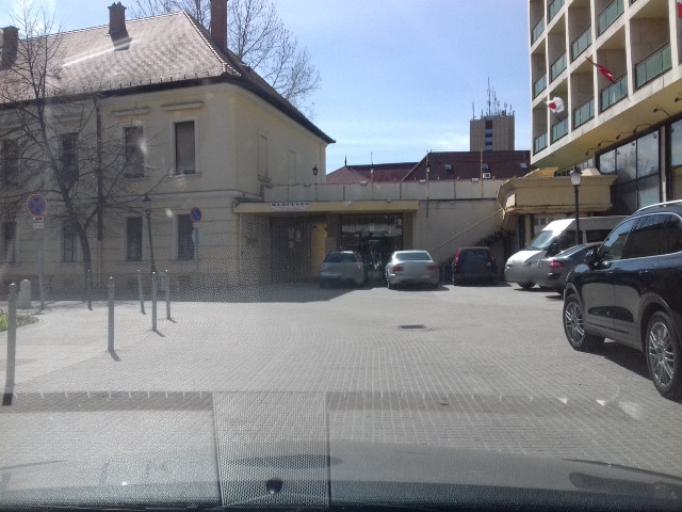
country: HU
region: Bacs-Kiskun
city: Kecskemet
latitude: 46.9081
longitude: 19.6909
